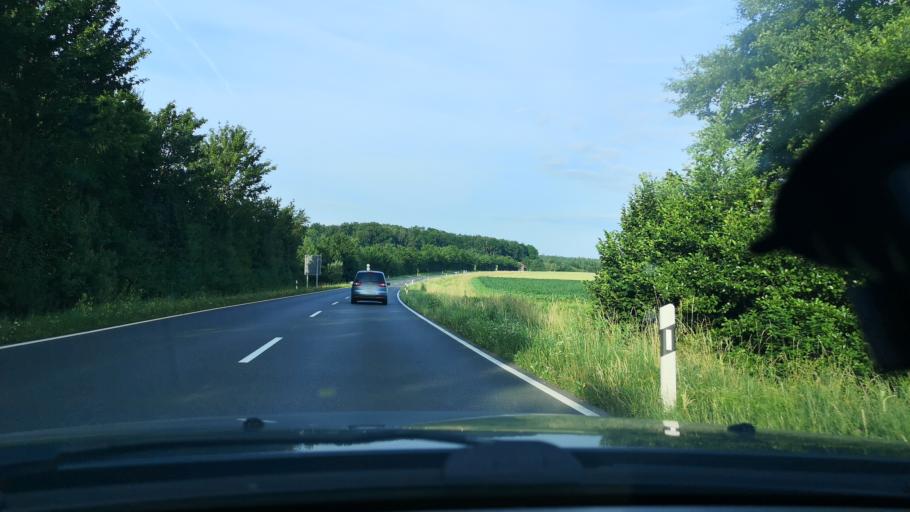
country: DE
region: Baden-Wuerttemberg
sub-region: Regierungsbezirk Stuttgart
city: Schlierbach
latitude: 48.6699
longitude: 9.5053
